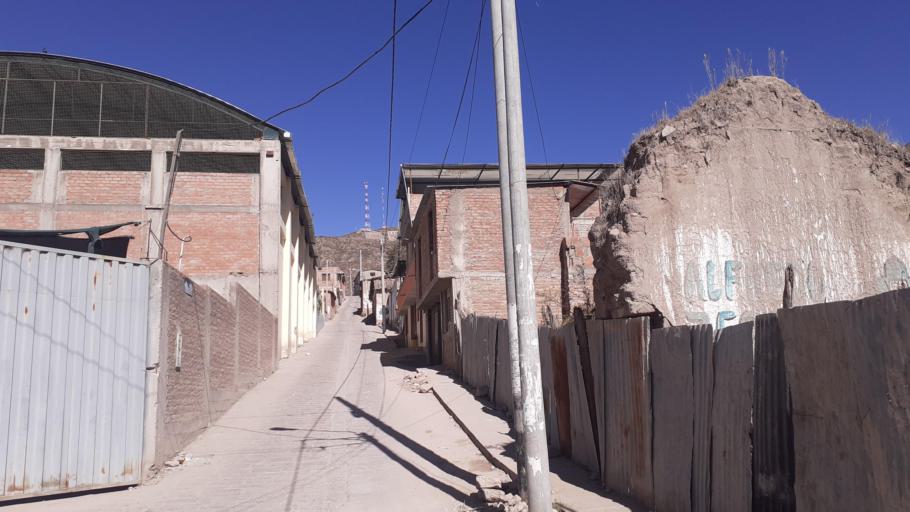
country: PE
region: Arequipa
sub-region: Provincia de Condesuyos
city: Chuquibamba
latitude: -15.8363
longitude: -72.6549
